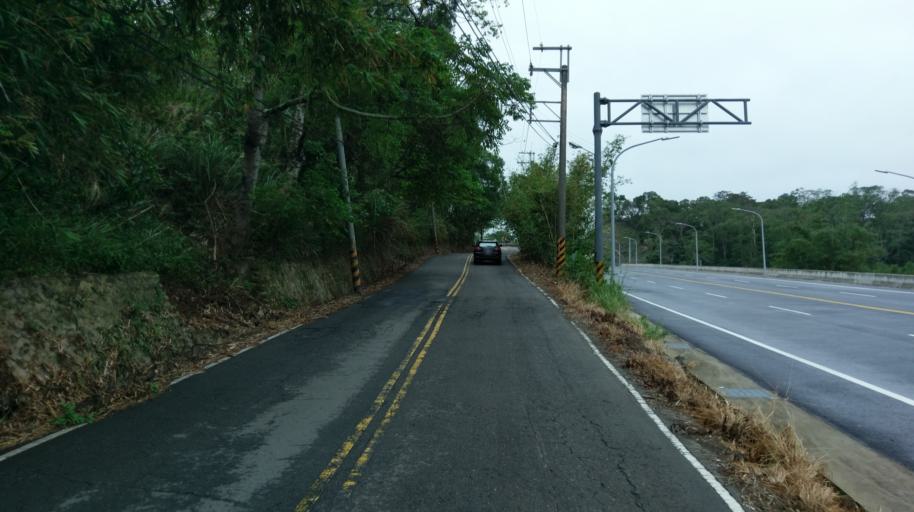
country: TW
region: Taiwan
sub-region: Hsinchu
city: Hsinchu
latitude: 24.7381
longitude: 120.9638
